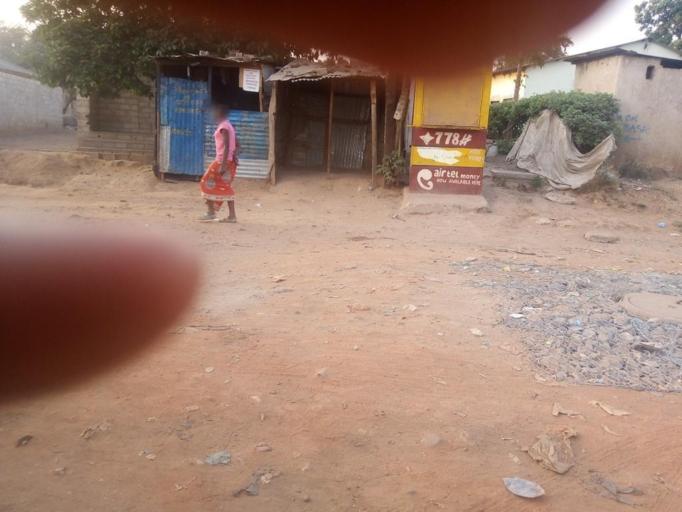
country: ZM
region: Lusaka
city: Lusaka
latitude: -15.4038
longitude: 28.3743
